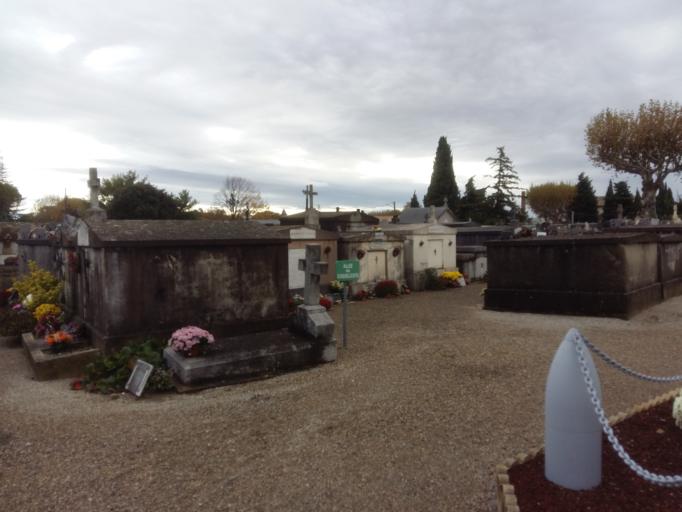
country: FR
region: Provence-Alpes-Cote d'Azur
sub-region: Departement du Vaucluse
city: Camaret-sur-Aigues
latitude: 44.1675
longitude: 4.8694
